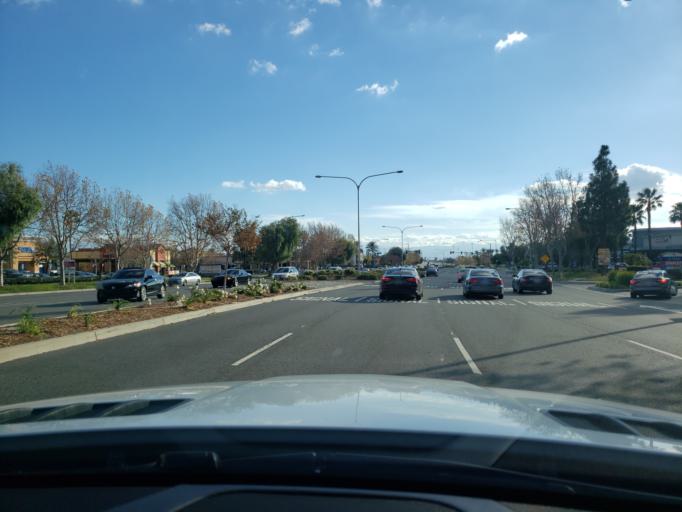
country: US
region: California
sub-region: San Bernardino County
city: Rancho Cucamonga
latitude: 34.0738
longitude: -117.5578
